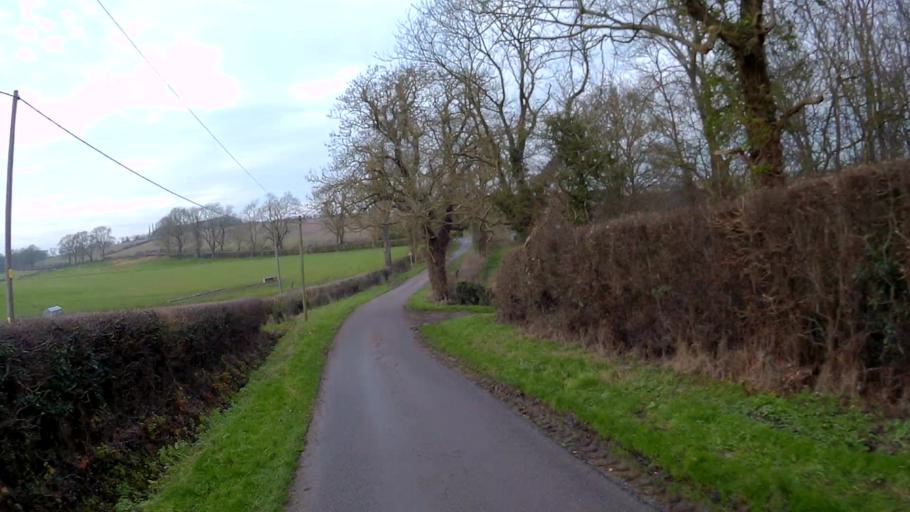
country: GB
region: England
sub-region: Lincolnshire
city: Bourne
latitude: 52.8266
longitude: -0.4607
